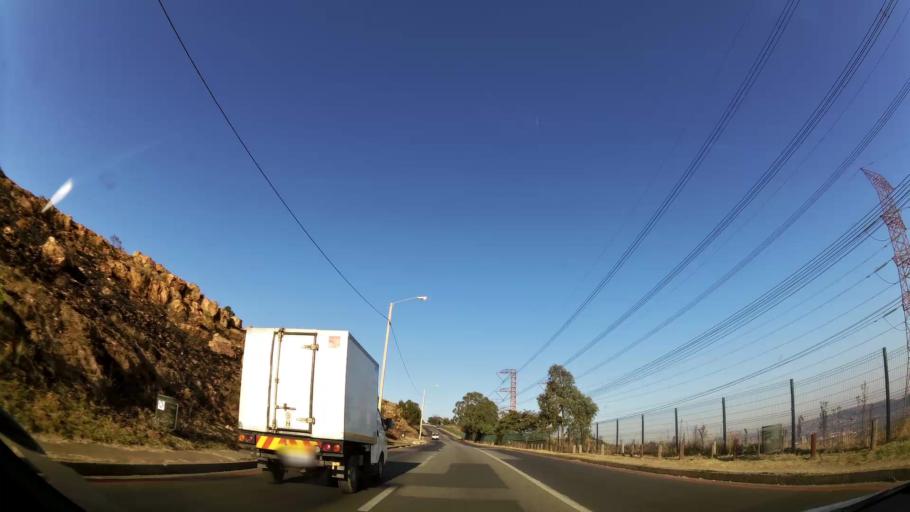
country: ZA
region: Gauteng
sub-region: Ekurhuleni Metropolitan Municipality
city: Germiston
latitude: -26.1780
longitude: 28.1578
